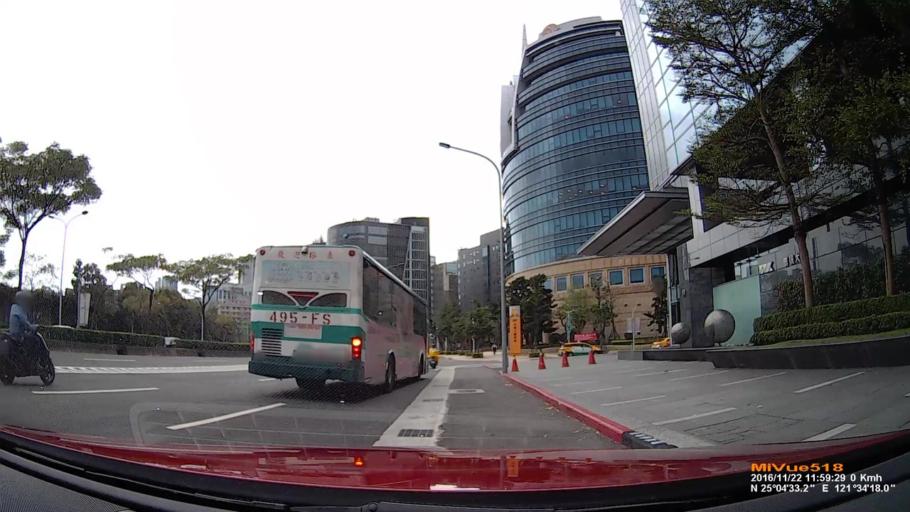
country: TW
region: Taipei
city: Taipei
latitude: 25.0759
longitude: 121.5717
